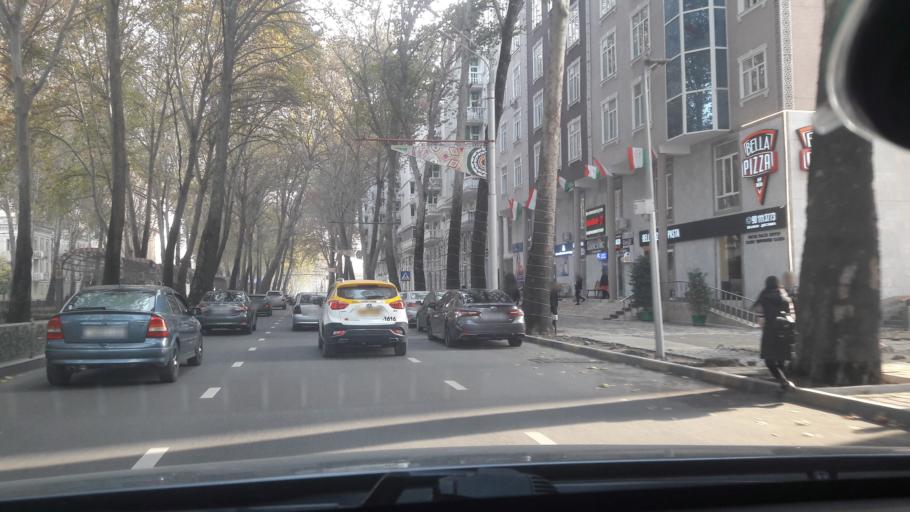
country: TJ
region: Dushanbe
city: Dushanbe
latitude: 38.5731
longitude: 68.7875
